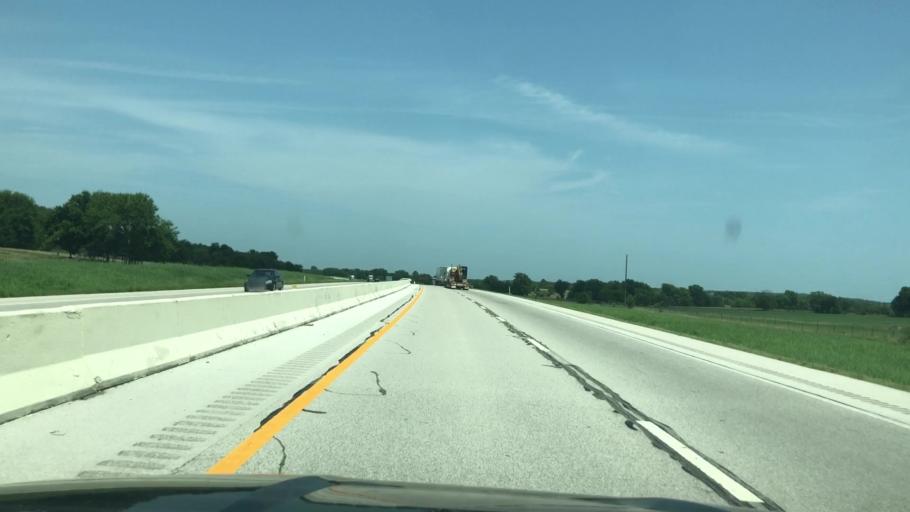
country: US
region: Oklahoma
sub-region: Rogers County
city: Bushyhead
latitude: 36.3513
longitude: -95.4632
